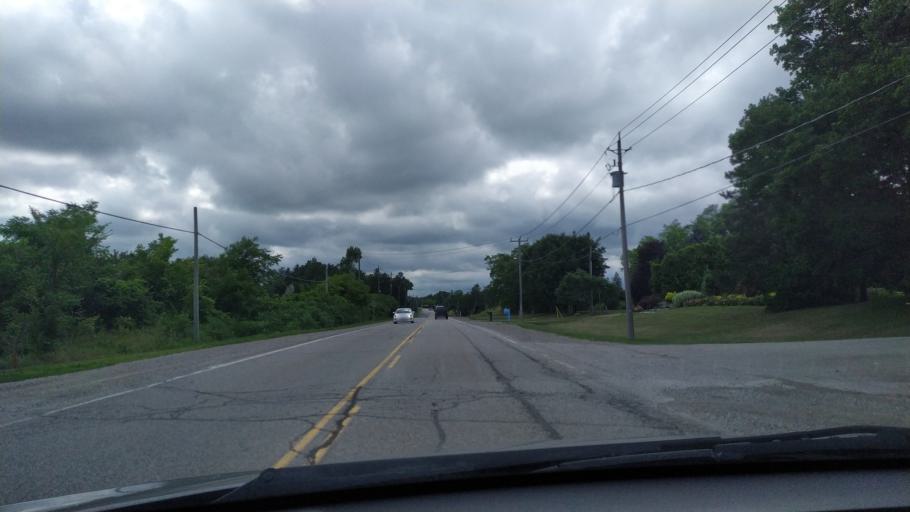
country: CA
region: Ontario
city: Cambridge
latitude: 43.3755
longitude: -80.4147
